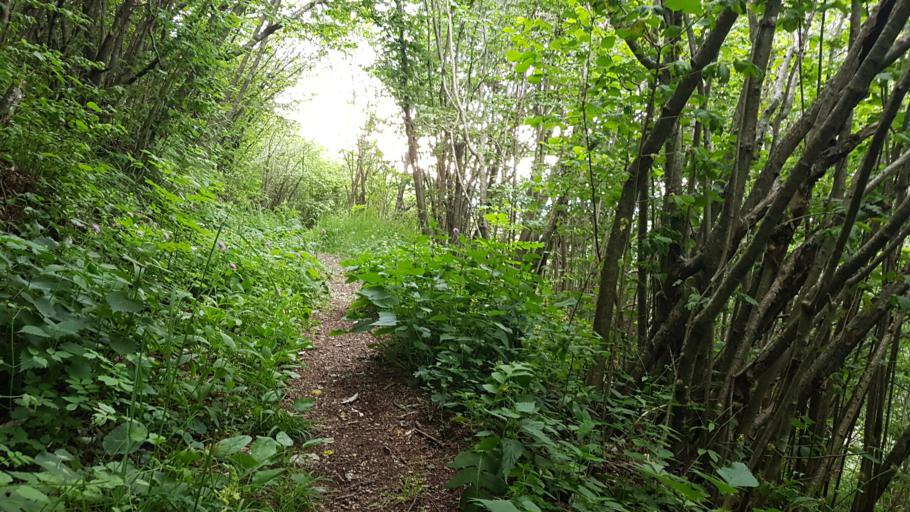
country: IT
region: Friuli Venezia Giulia
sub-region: Provincia di Udine
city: Taipana
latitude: 46.2838
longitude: 13.3249
